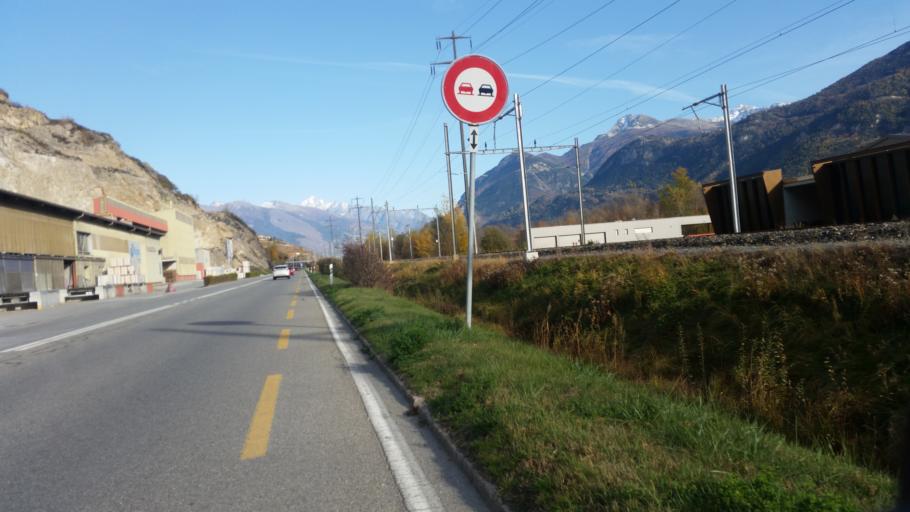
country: CH
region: Valais
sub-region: Sierre District
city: Grone
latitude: 46.2615
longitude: 7.4481
